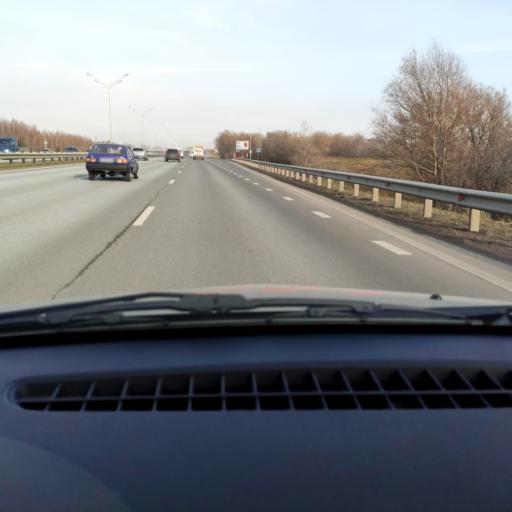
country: RU
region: Bashkortostan
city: Ufa
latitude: 54.6129
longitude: 55.9252
